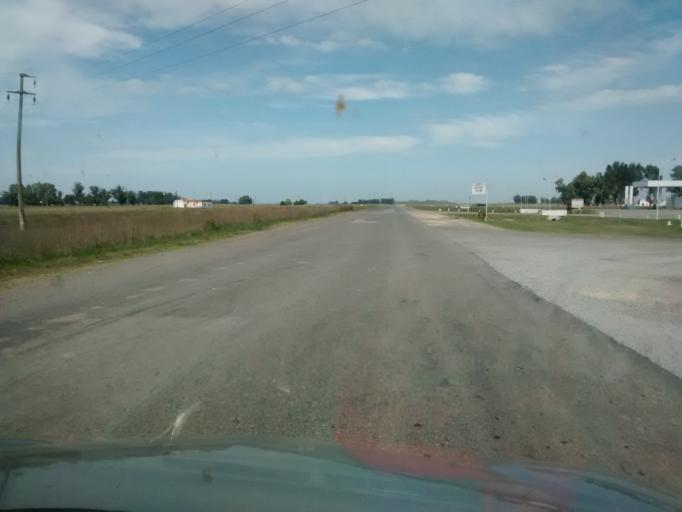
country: AR
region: Buenos Aires
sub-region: Partido de Ayacucho
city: Ayacucho
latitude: -37.1308
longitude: -58.5519
